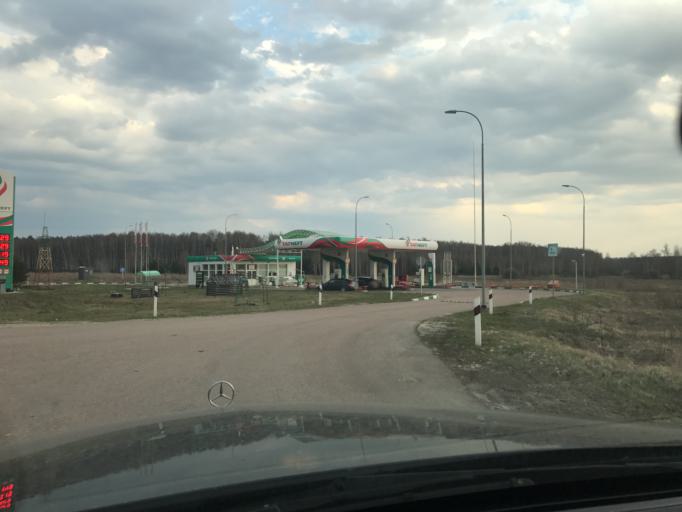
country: RU
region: Vladimir
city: Murom
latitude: 55.6235
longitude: 41.9004
